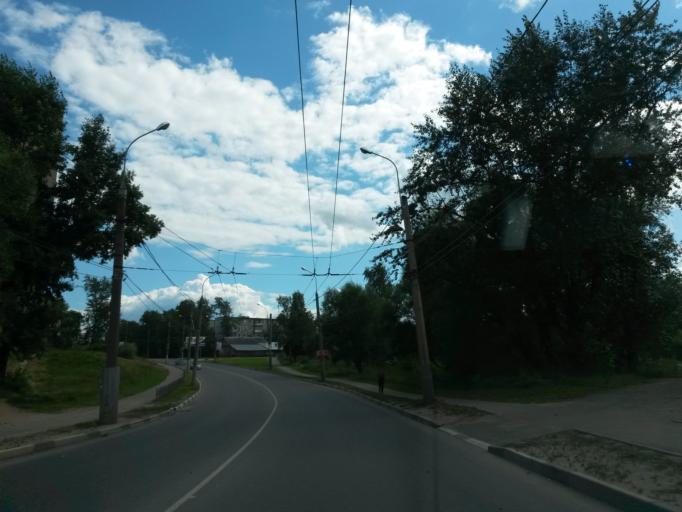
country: RU
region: Ivanovo
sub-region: Gorod Ivanovo
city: Ivanovo
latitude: 56.9839
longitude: 40.9941
